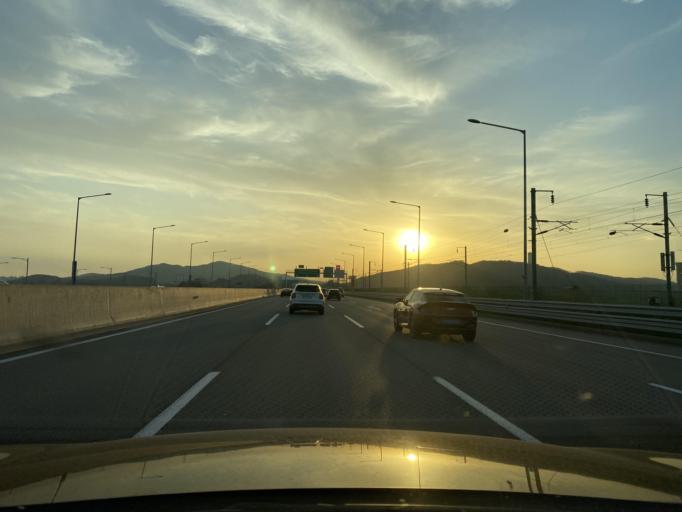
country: KR
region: Incheon
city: Incheon
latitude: 37.5254
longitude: 126.5469
